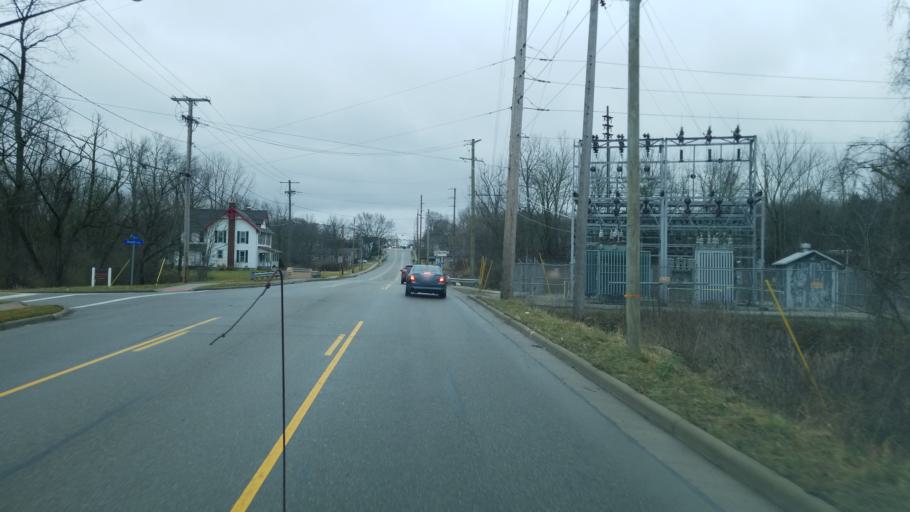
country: US
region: Ohio
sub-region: Summit County
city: Norton
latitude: 41.0105
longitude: -81.6386
